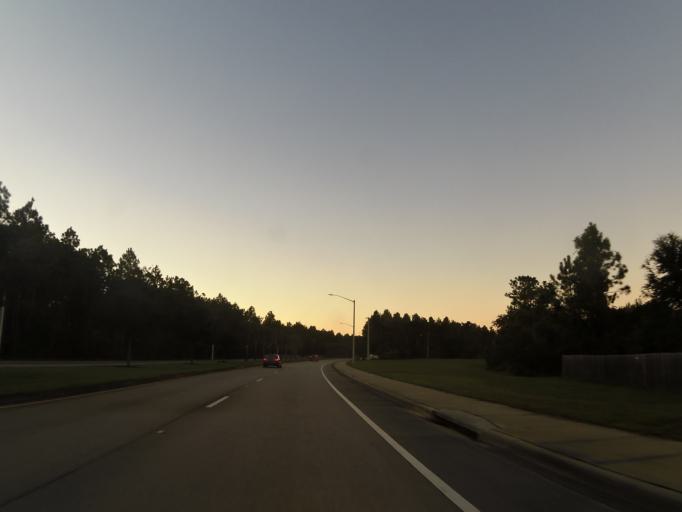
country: US
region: Florida
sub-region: Flagler County
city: Palm Coast
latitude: 29.5930
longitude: -81.2645
